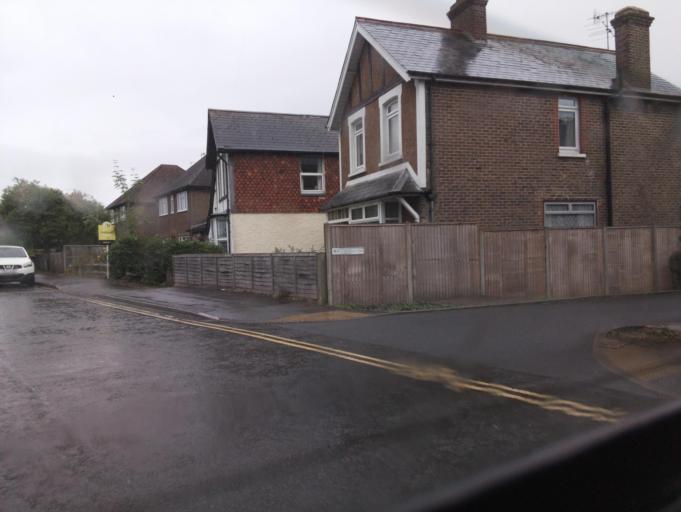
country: GB
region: England
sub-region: Surrey
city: Salfords
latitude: 51.2154
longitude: -0.1705
